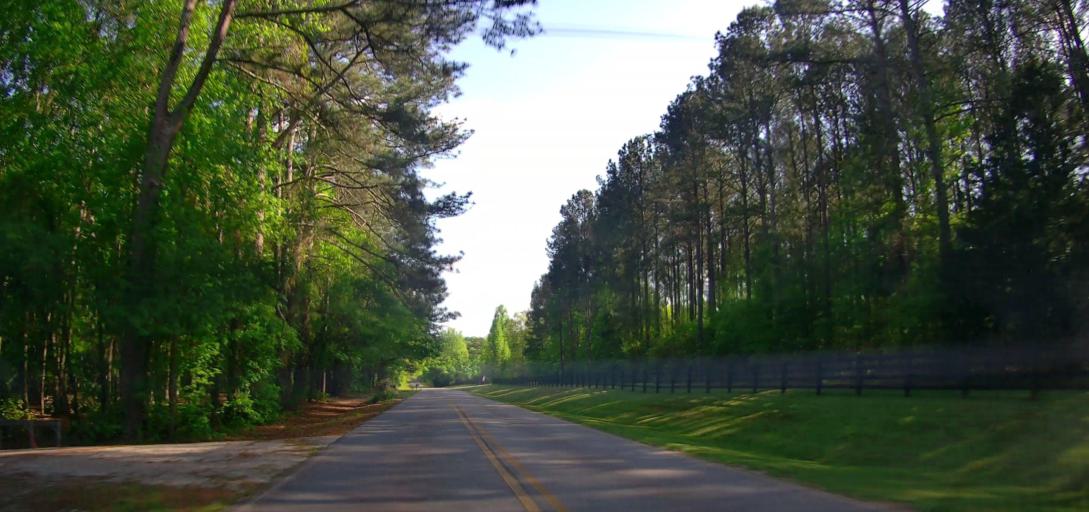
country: US
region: Georgia
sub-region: Morgan County
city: Madison
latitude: 33.5318
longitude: -83.4789
